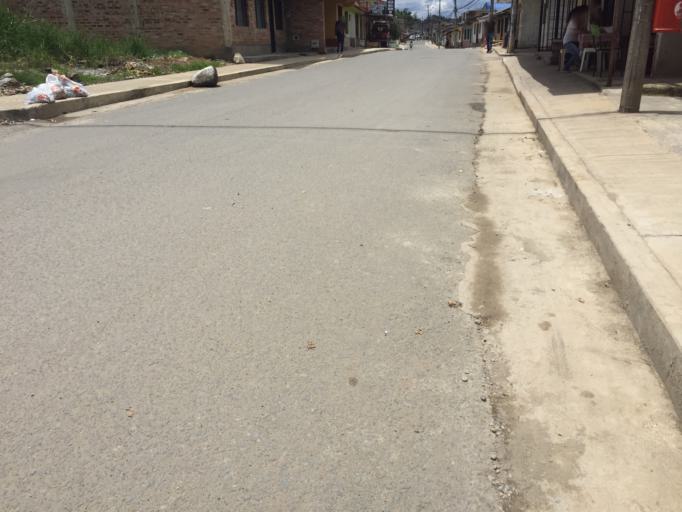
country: CO
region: Cauca
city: Popayan
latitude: 2.4549
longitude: -76.5865
